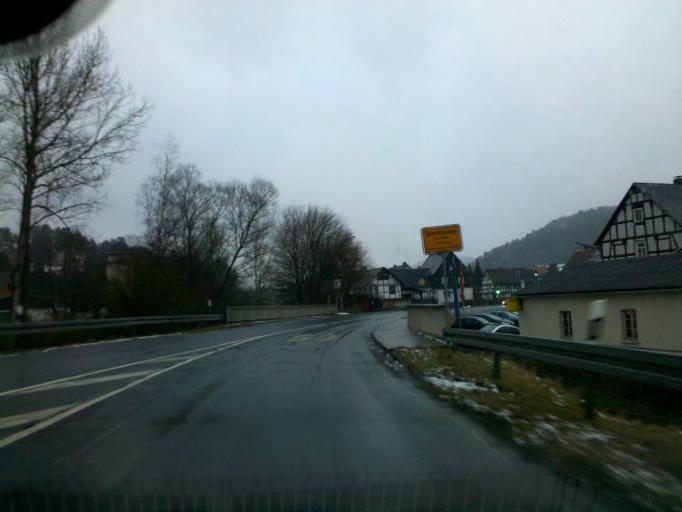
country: DE
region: Hesse
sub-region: Regierungsbezirk Giessen
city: Breidenbach
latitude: 50.8558
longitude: 8.4699
